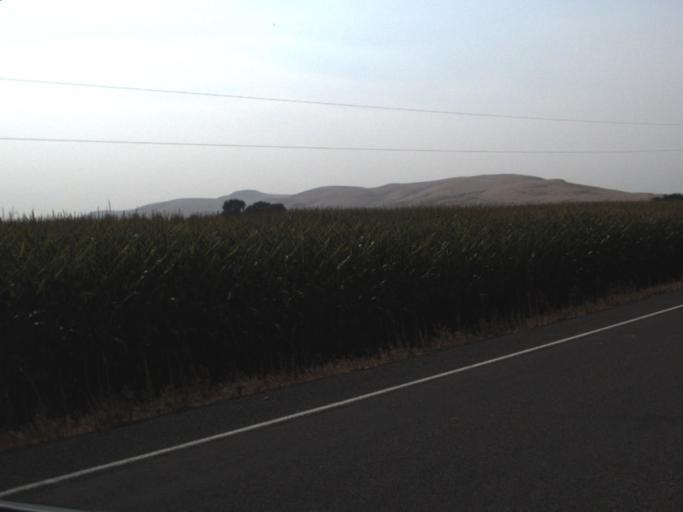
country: US
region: Washington
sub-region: Yakima County
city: Granger
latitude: 46.2961
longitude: -120.1886
